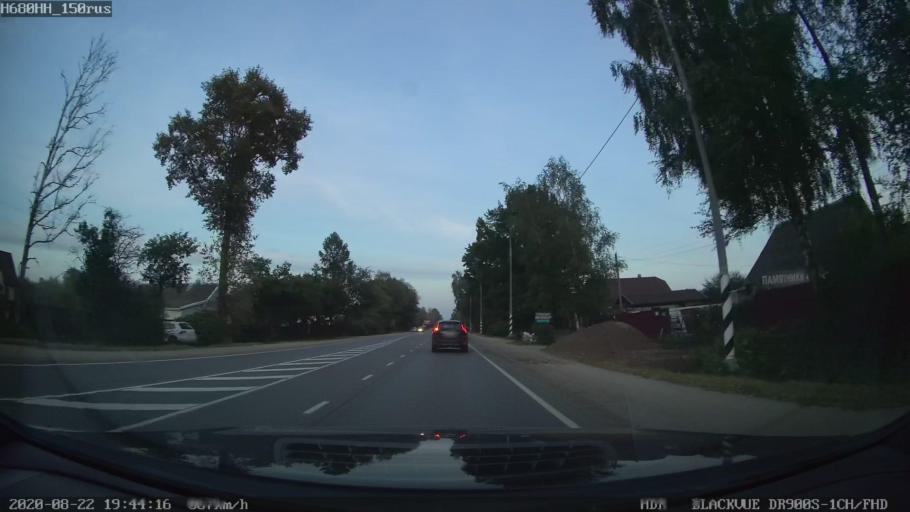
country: RU
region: Tverskaya
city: Emmaus
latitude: 56.7908
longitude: 36.0716
